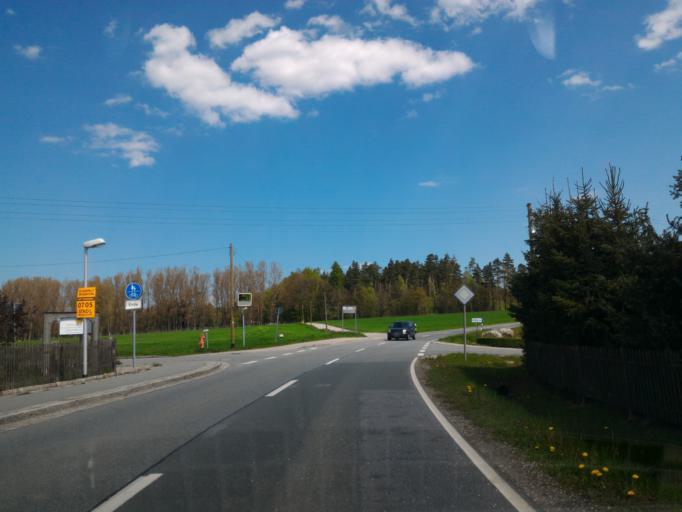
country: DE
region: Saxony
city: Leutersdorf
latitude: 50.9489
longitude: 14.6753
